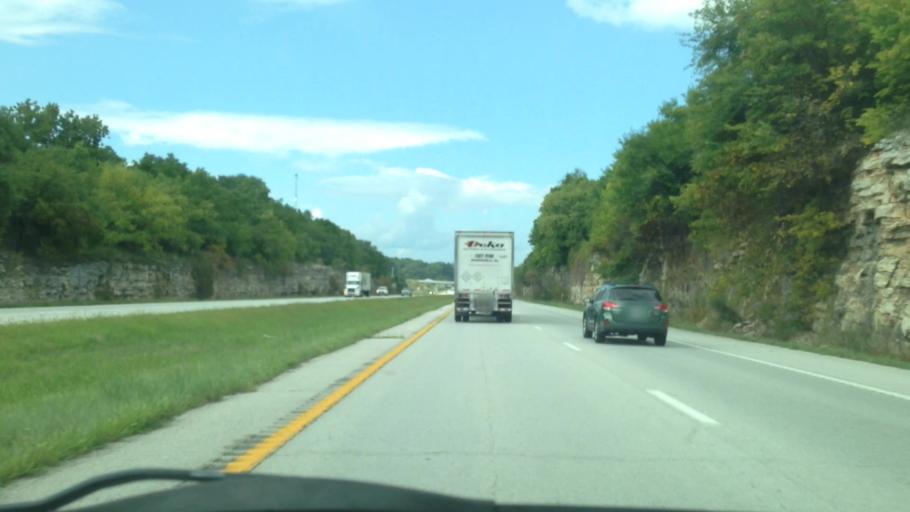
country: US
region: Missouri
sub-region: Marion County
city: Palmyra
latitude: 39.8035
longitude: -91.5163
